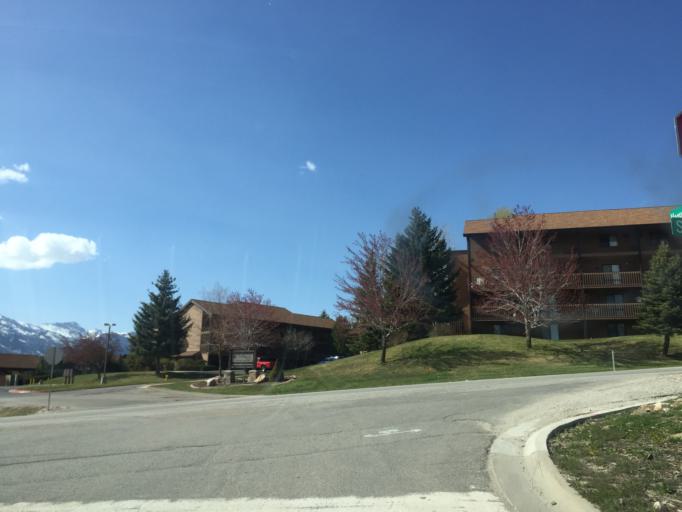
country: US
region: Utah
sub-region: Weber County
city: Wolf Creek
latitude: 41.3244
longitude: -111.8282
